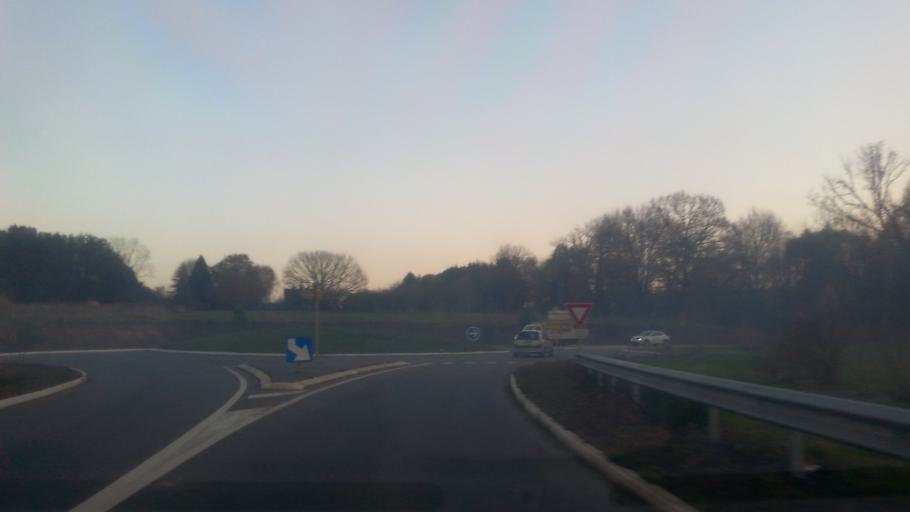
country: FR
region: Brittany
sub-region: Departement d'Ille-et-Vilaine
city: Bains-sur-Oust
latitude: 47.6893
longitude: -2.0559
